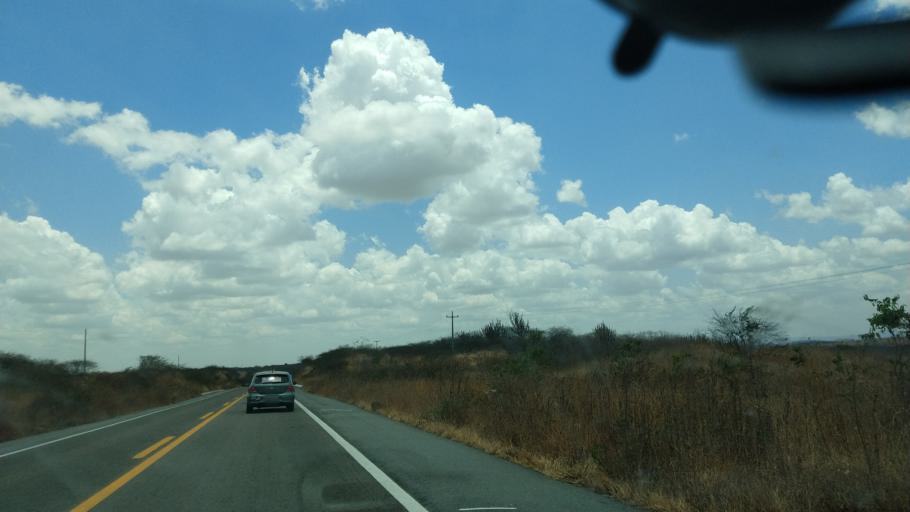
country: BR
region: Rio Grande do Norte
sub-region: Cerro Cora
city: Cerro Cora
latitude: -6.2004
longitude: -36.2719
